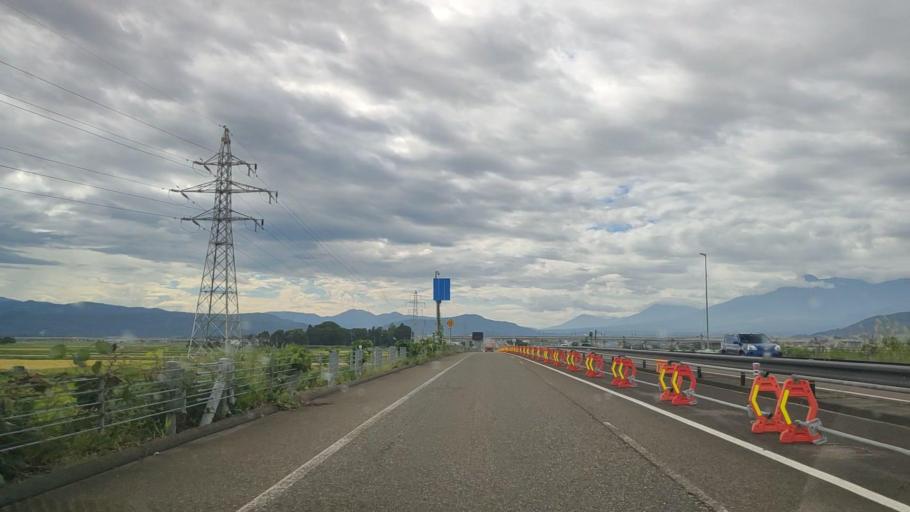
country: JP
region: Niigata
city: Joetsu
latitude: 37.0775
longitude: 138.2656
